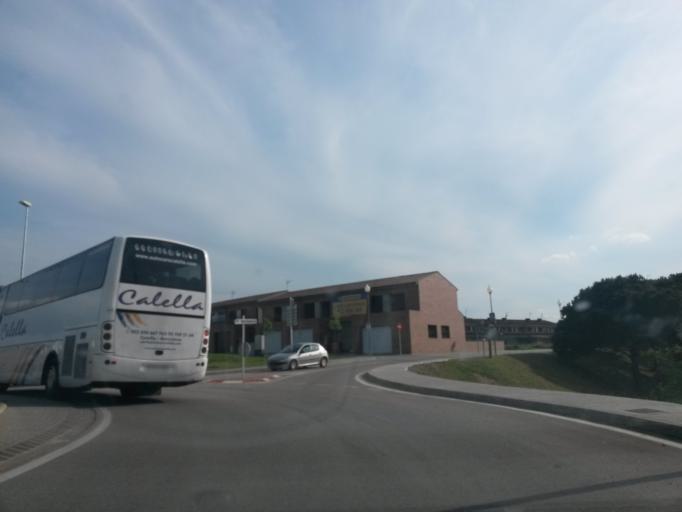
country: ES
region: Catalonia
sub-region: Provincia de Girona
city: Vidreres
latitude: 41.7944
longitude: 2.7765
